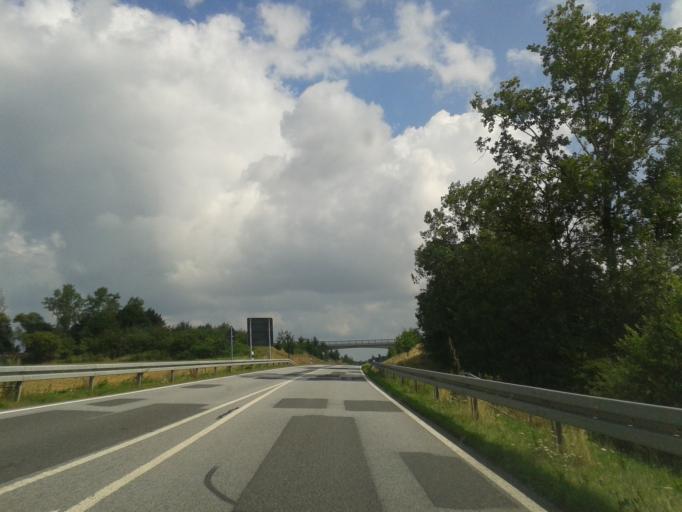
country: DE
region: Saxony
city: Goda
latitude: 51.1983
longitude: 14.3667
